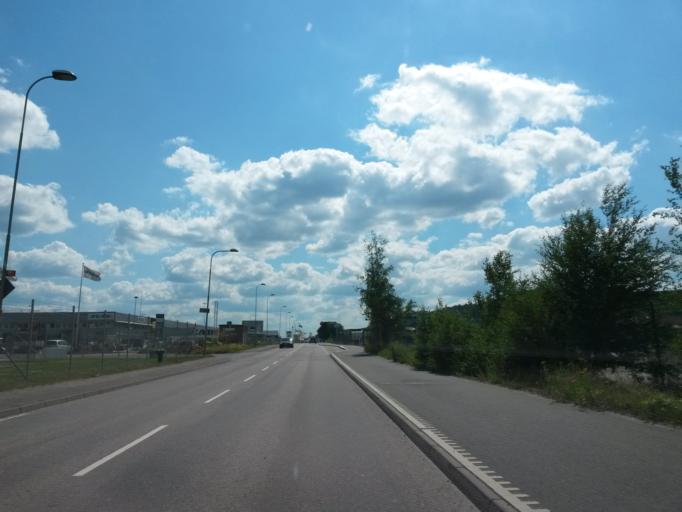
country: SE
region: Vaestra Goetaland
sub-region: Goteborg
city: Hammarkullen
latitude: 57.7779
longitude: 11.9941
